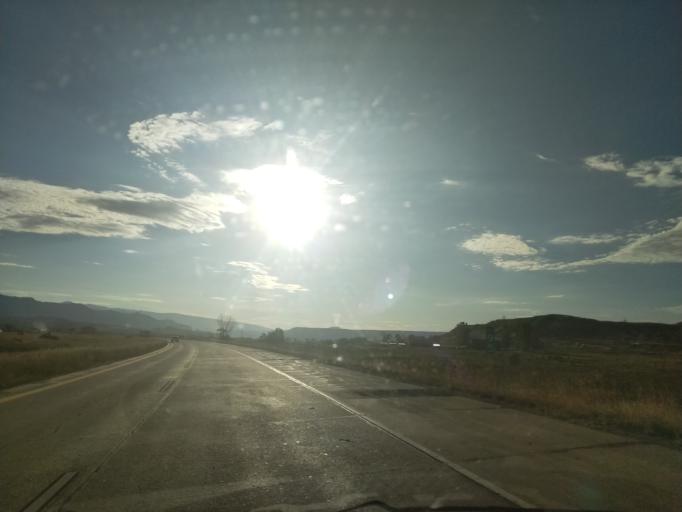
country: US
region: Colorado
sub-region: Garfield County
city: Silt
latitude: 39.5321
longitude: -107.6951
